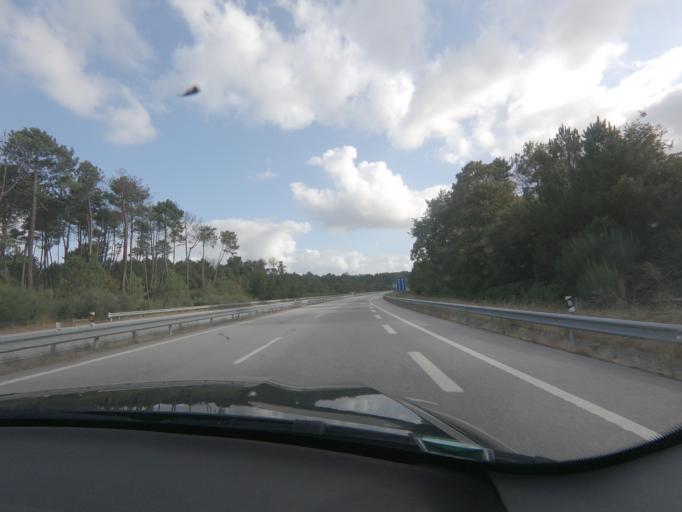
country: PT
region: Viseu
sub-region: Viseu
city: Campo
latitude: 40.7252
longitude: -7.9224
